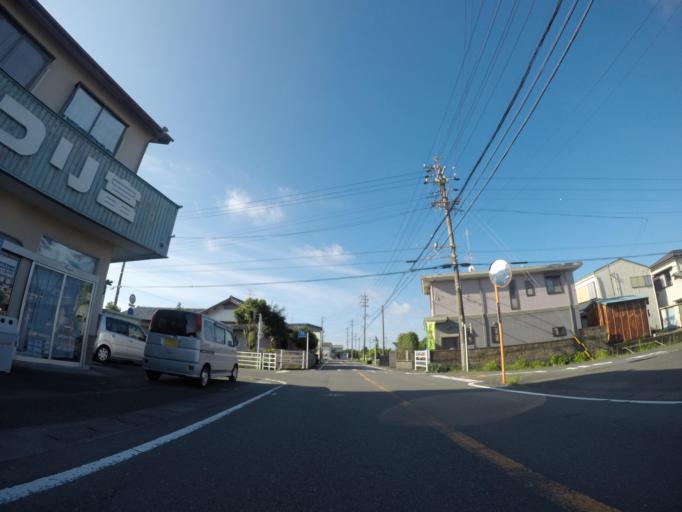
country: JP
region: Shizuoka
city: Yaizu
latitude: 34.8341
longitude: 138.3118
